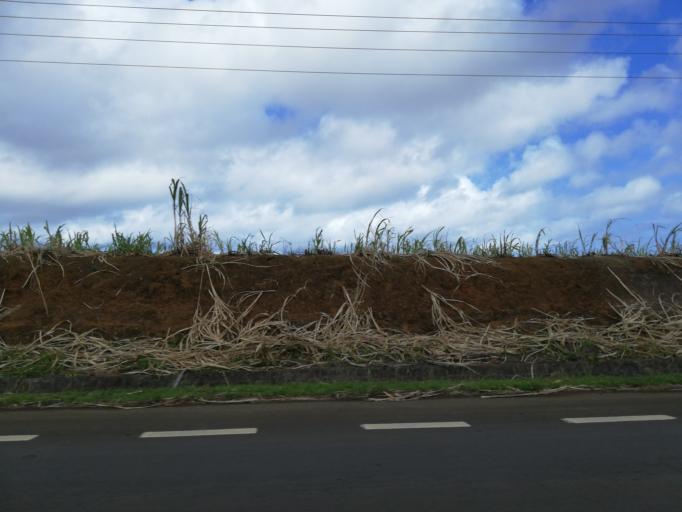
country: MU
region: Grand Port
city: Plaine Magnien
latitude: -20.4177
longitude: 57.6701
